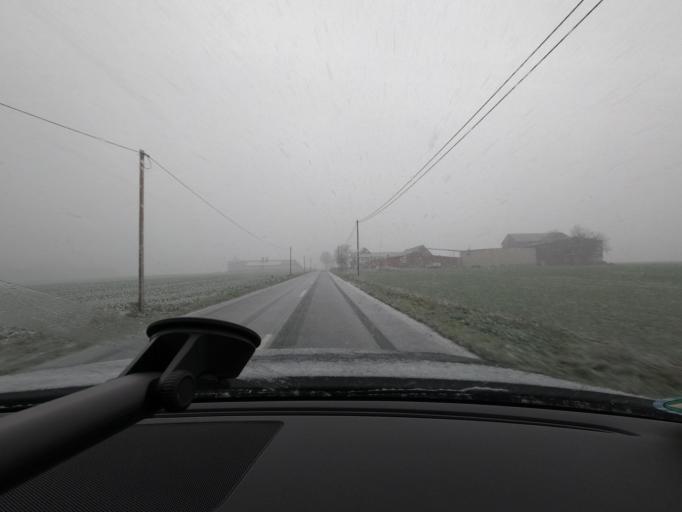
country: DE
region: North Rhine-Westphalia
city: Marsberg
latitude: 51.5355
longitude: 8.8409
